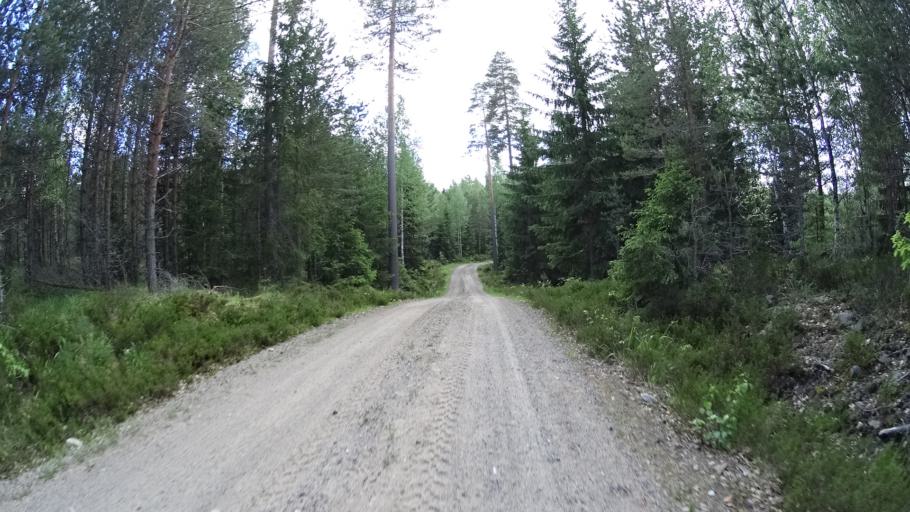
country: FI
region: Varsinais-Suomi
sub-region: Salo
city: Kisko
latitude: 60.1878
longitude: 23.5521
